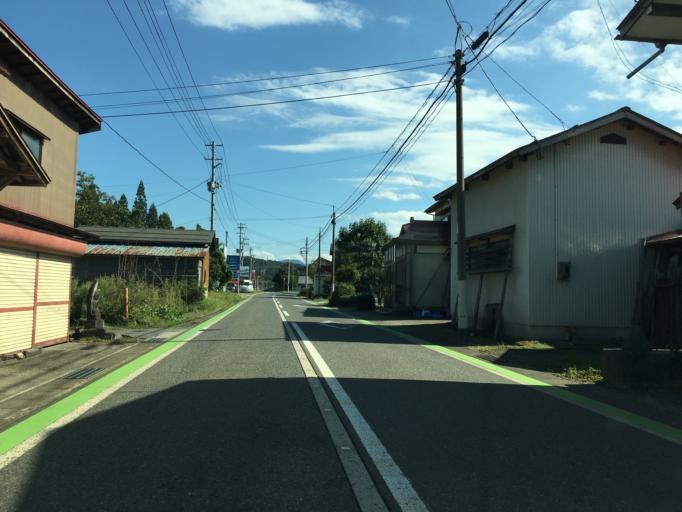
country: JP
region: Niigata
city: Suibara
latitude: 37.6689
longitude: 139.4693
